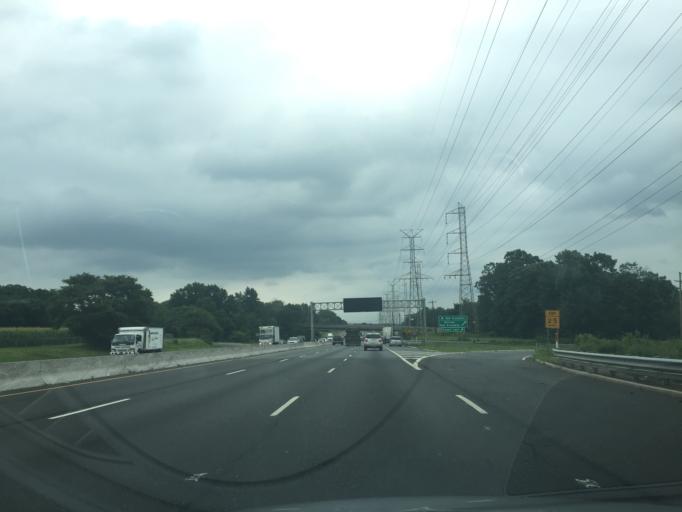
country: US
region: New Jersey
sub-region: Middlesex County
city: Milltown
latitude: 40.4724
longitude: -74.4303
